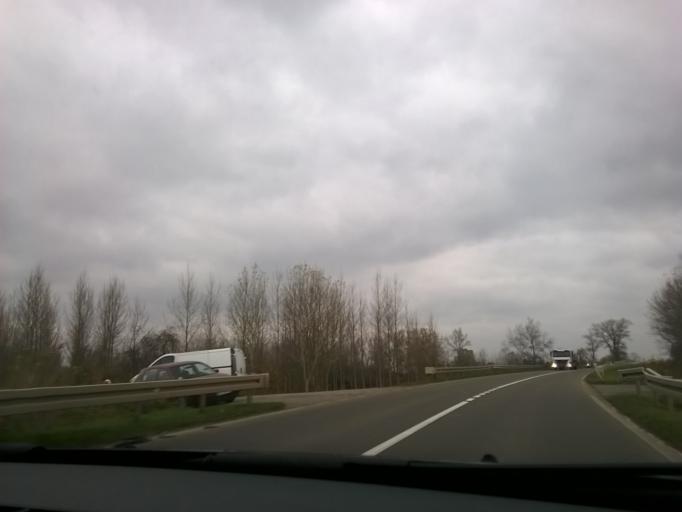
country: RS
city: Centa
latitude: 45.0944
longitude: 20.3754
